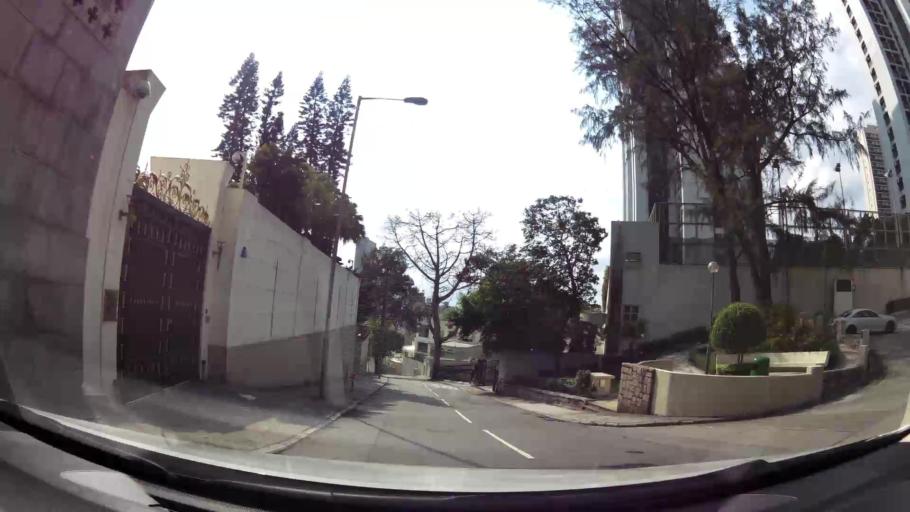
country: HK
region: Wanchai
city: Wan Chai
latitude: 22.2697
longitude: 114.1934
